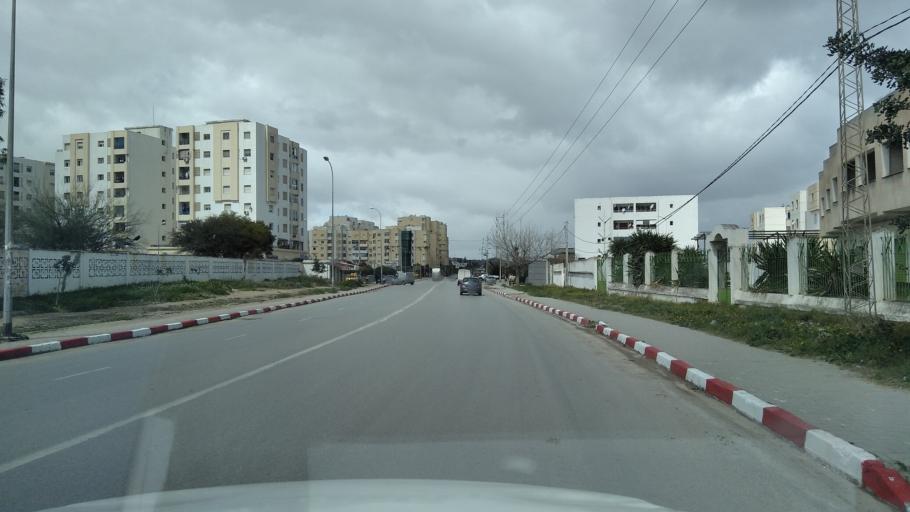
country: TN
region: Bin 'Arus
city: Ben Arous
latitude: 36.7461
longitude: 10.2328
